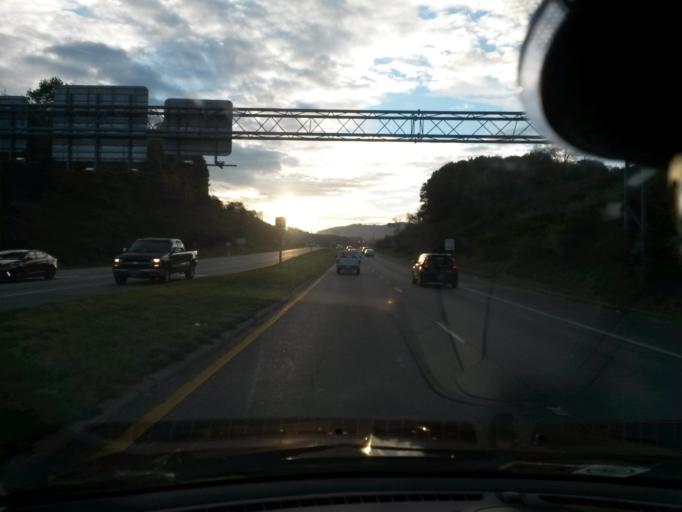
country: US
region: Virginia
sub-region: Botetourt County
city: Cloverdale
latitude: 37.3868
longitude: -79.9017
